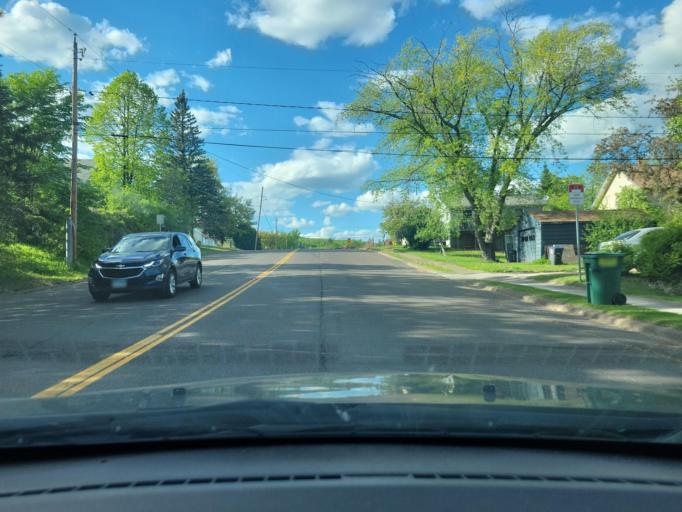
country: US
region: Minnesota
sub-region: Saint Louis County
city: Arnold
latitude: 46.8387
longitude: -92.0293
